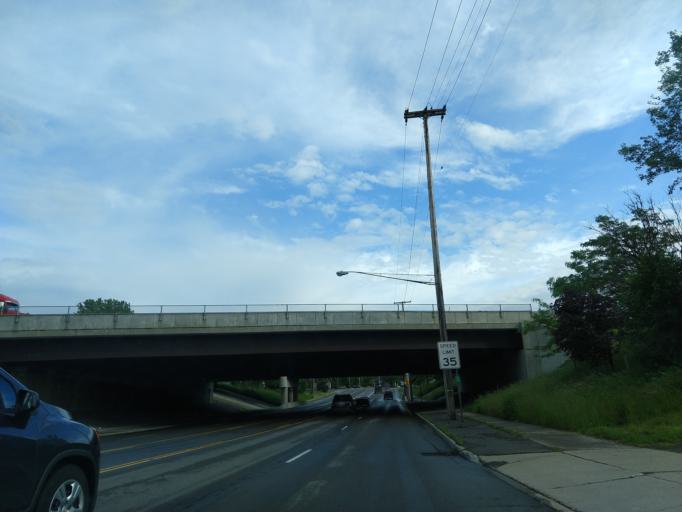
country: US
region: New York
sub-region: Erie County
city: Sloan
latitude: 42.8771
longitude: -78.7849
